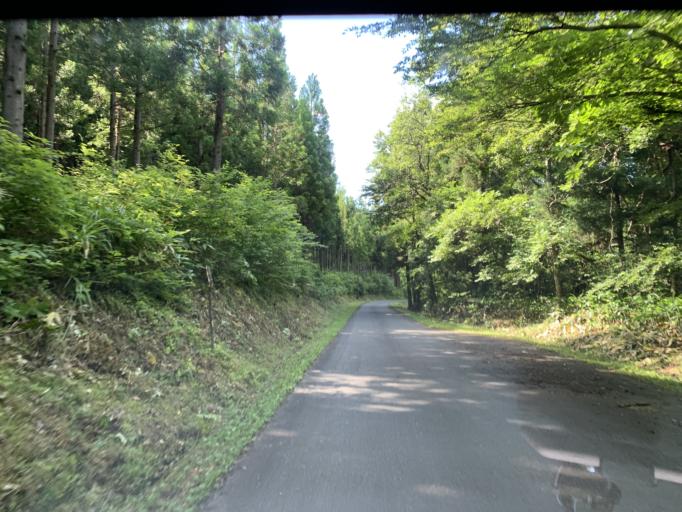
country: JP
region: Iwate
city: Ichinoseki
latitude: 38.9237
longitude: 140.9566
